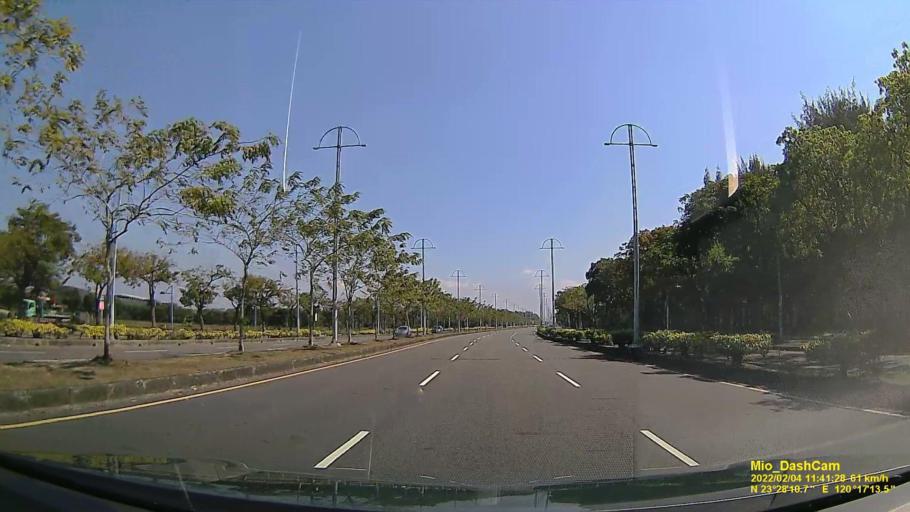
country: TW
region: Taiwan
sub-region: Chiayi
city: Taibao
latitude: 23.4696
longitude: 120.2872
